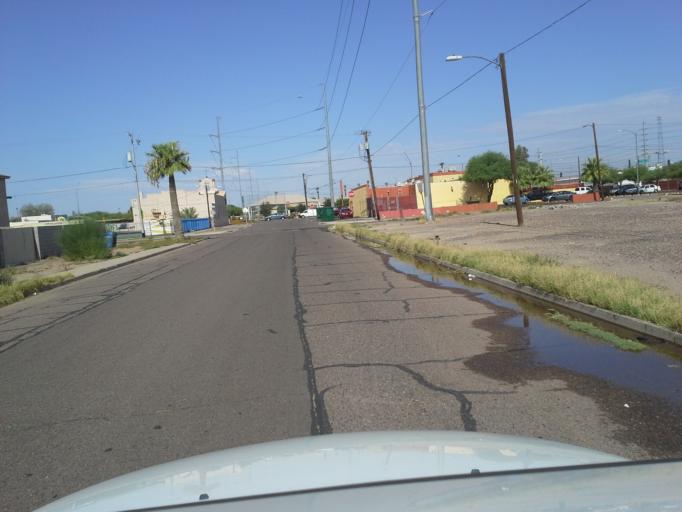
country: US
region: Arizona
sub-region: Maricopa County
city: Phoenix
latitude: 33.4401
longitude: -112.0807
